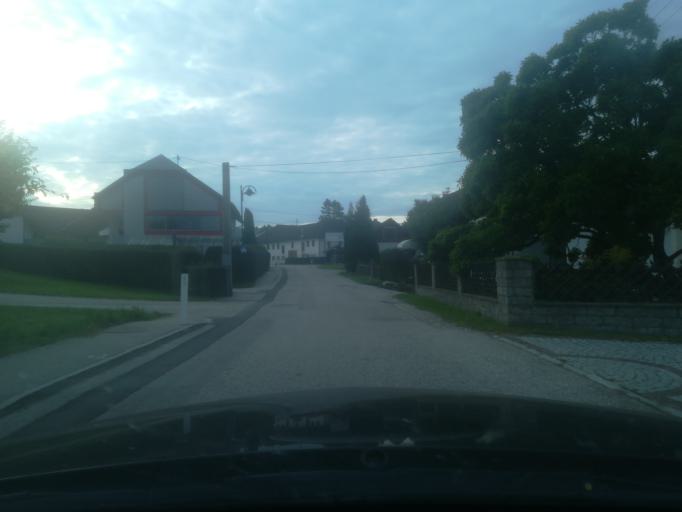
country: AT
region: Upper Austria
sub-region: Wels-Land
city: Buchkirchen
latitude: 48.2586
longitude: 14.0404
